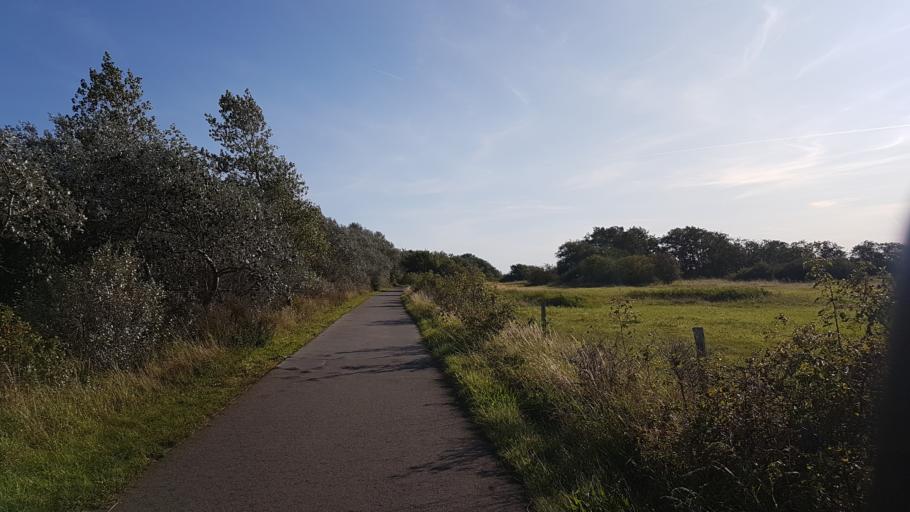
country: DE
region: Mecklenburg-Vorpommern
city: Wiek
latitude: 54.6379
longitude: 13.2912
